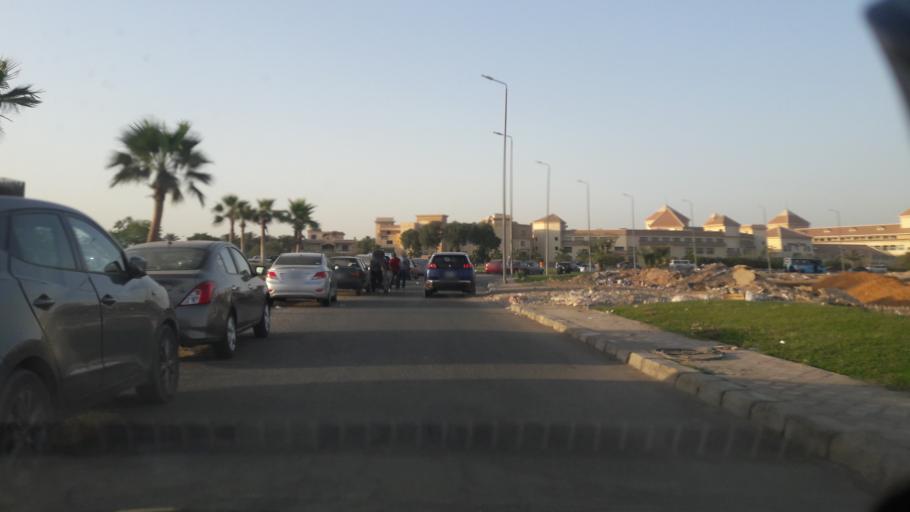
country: EG
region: Al Jizah
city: Madinat Sittah Uktubar
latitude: 29.9608
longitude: 31.0421
